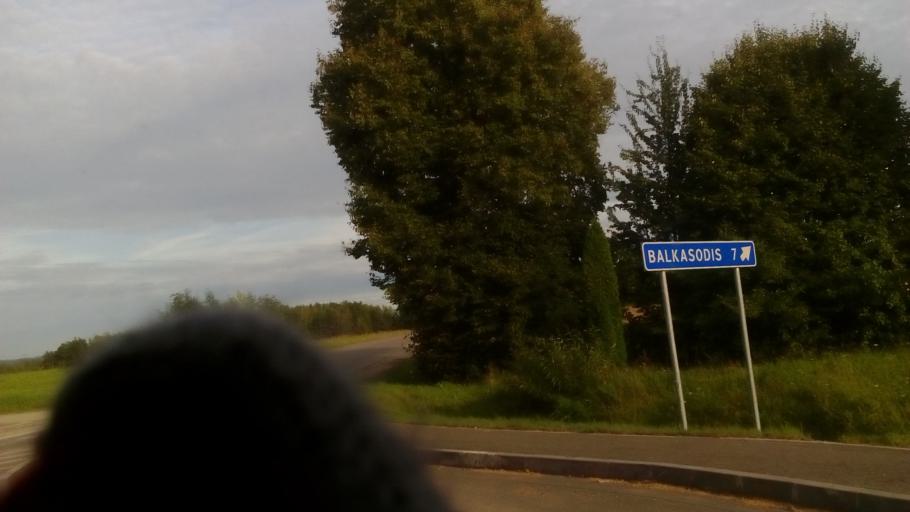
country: LT
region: Alytaus apskritis
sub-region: Alytus
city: Alytus
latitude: 54.3249
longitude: 23.9267
